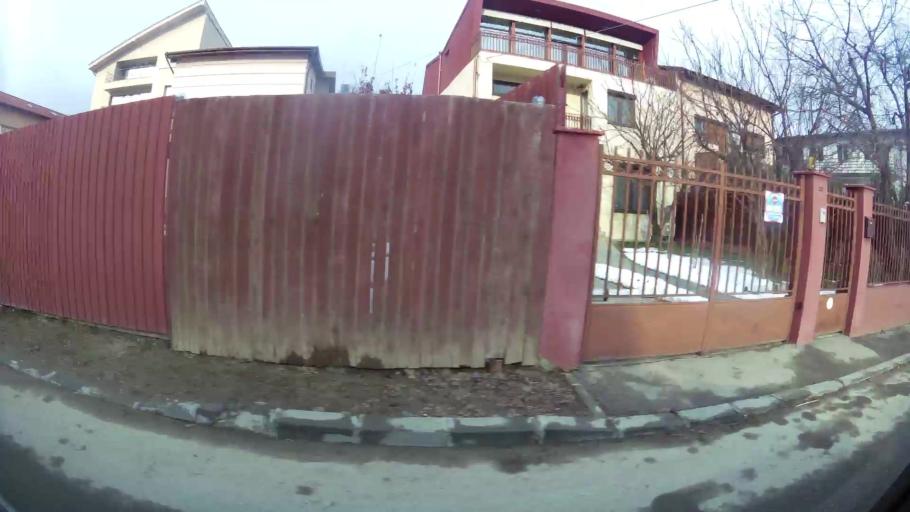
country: RO
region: Ilfov
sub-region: Comuna Popesti-Leordeni
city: Popesti-Leordeni
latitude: 44.4013
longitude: 26.1743
